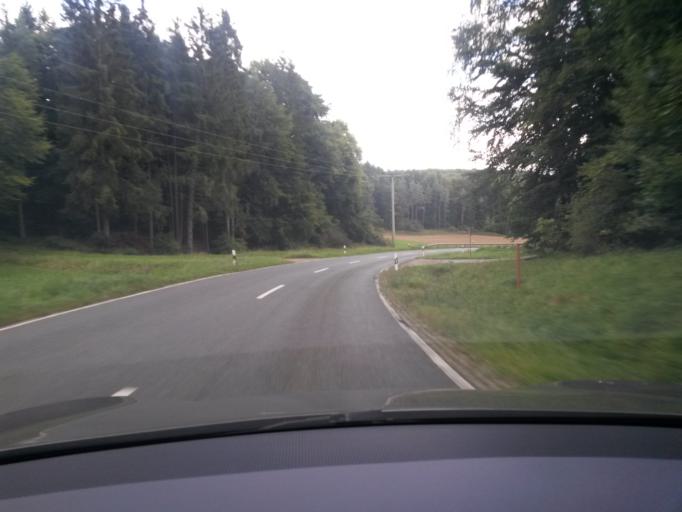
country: DE
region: Bavaria
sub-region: Upper Palatinate
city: Hohenfels
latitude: 49.1862
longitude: 11.8248
